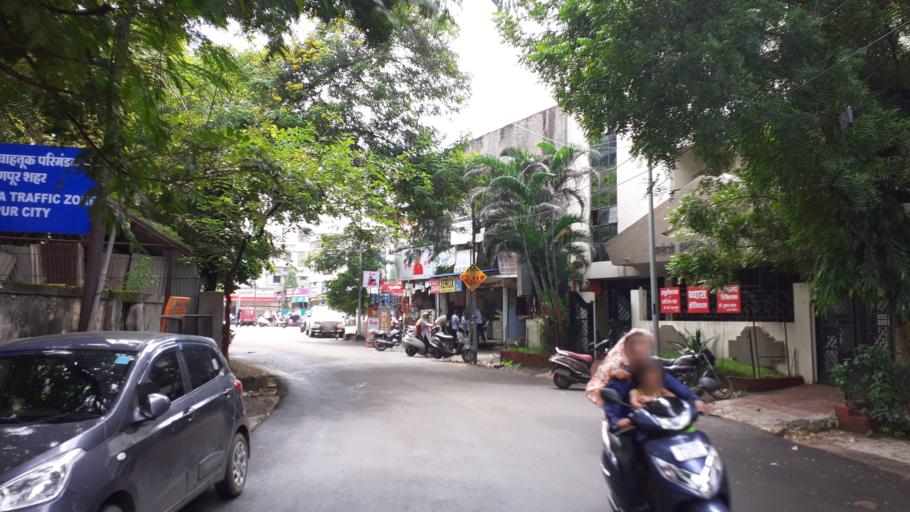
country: IN
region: Maharashtra
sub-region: Nagpur Division
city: Nagpur
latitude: 21.1296
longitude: 79.1138
